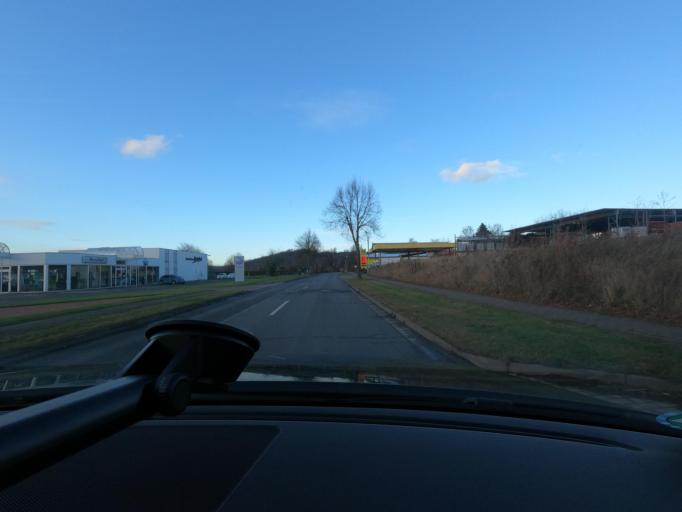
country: DE
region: Lower Saxony
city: Rhumspringe
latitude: 51.5779
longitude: 10.2953
